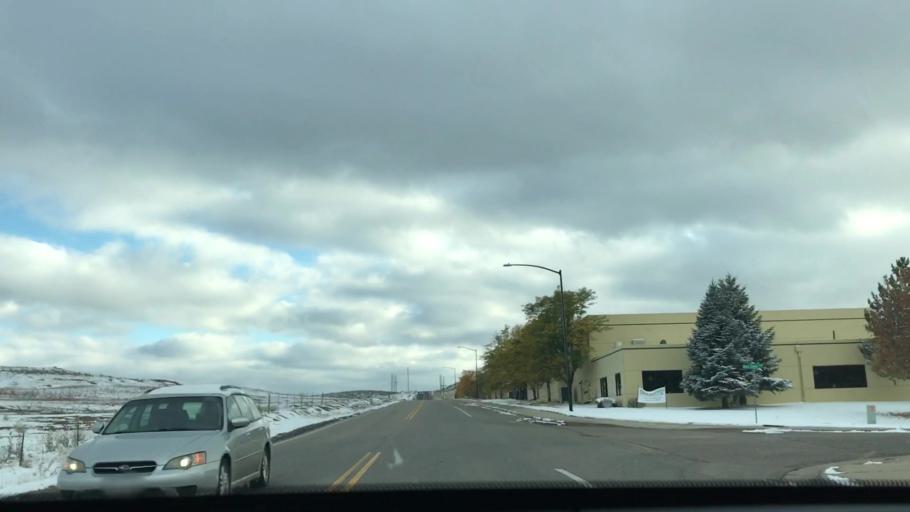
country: US
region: Colorado
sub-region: Boulder County
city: Lafayette
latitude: 39.9753
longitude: -105.0719
